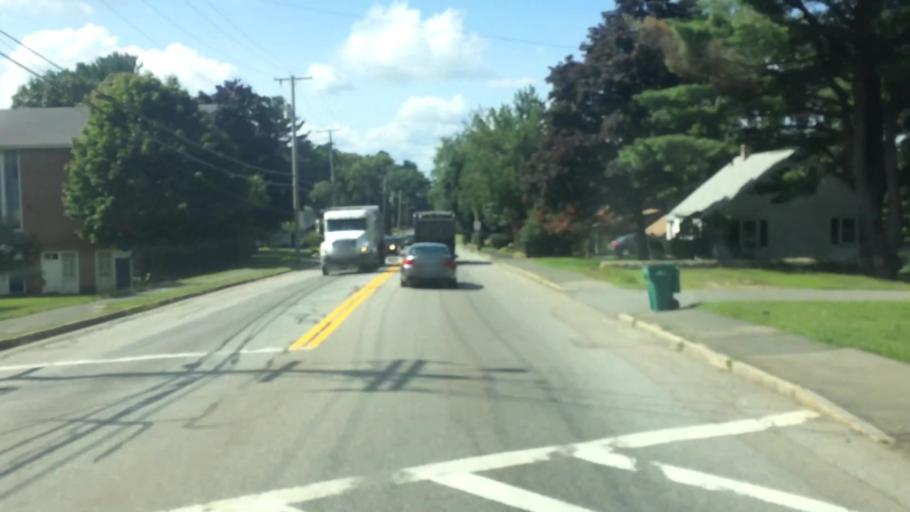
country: US
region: Massachusetts
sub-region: Essex County
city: South Peabody
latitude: 42.5060
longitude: -70.9829
